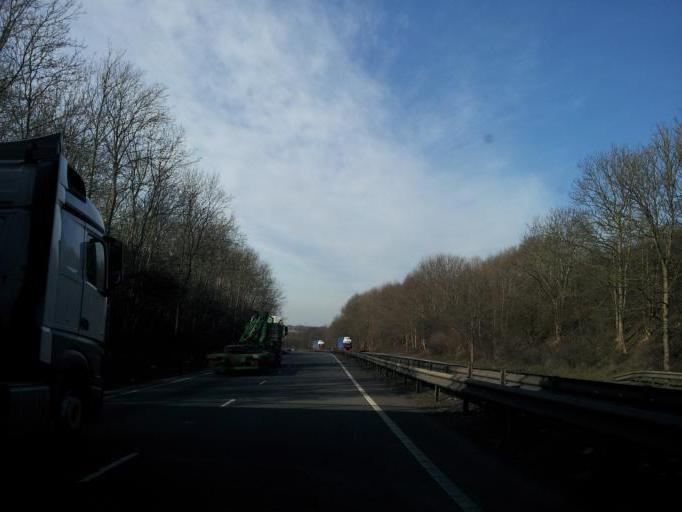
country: GB
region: England
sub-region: Lincolnshire
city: Grantham
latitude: 52.8920
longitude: -0.6493
